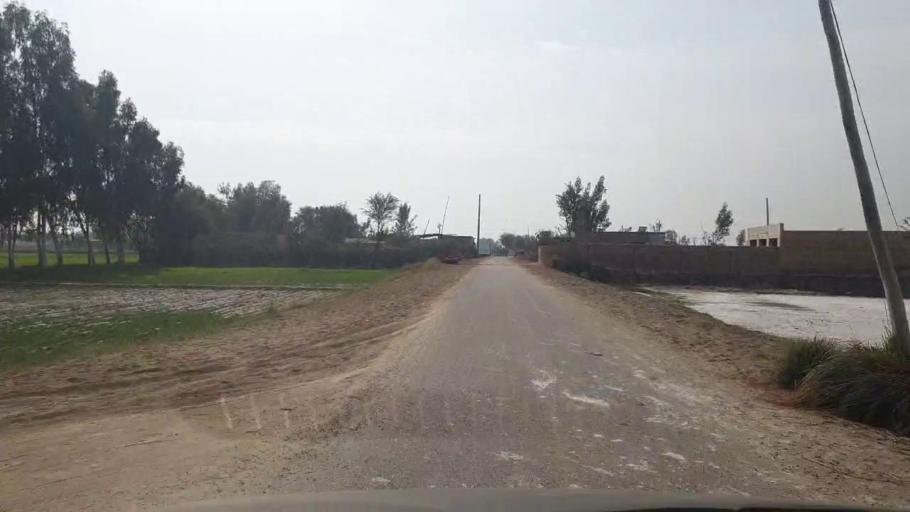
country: PK
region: Sindh
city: Hala
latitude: 25.9881
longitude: 68.4228
